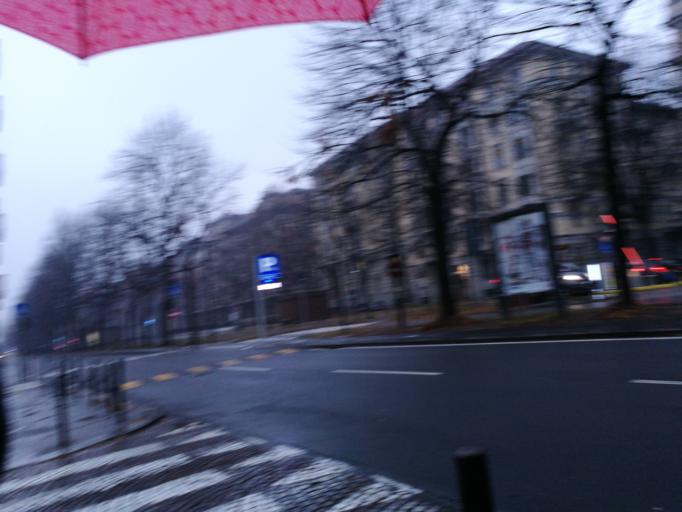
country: IT
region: Piedmont
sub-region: Provincia di Torino
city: Turin
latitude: 45.0694
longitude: 7.6737
